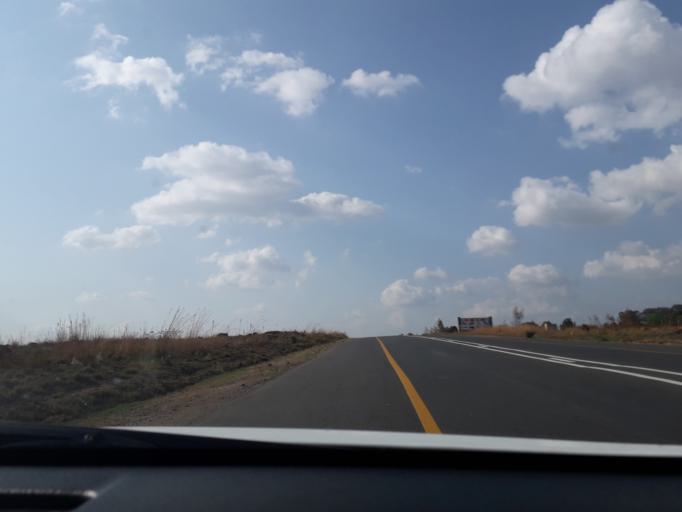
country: ZA
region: Gauteng
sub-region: City of Tshwane Metropolitan Municipality
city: Centurion
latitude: -25.9067
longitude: 28.2470
